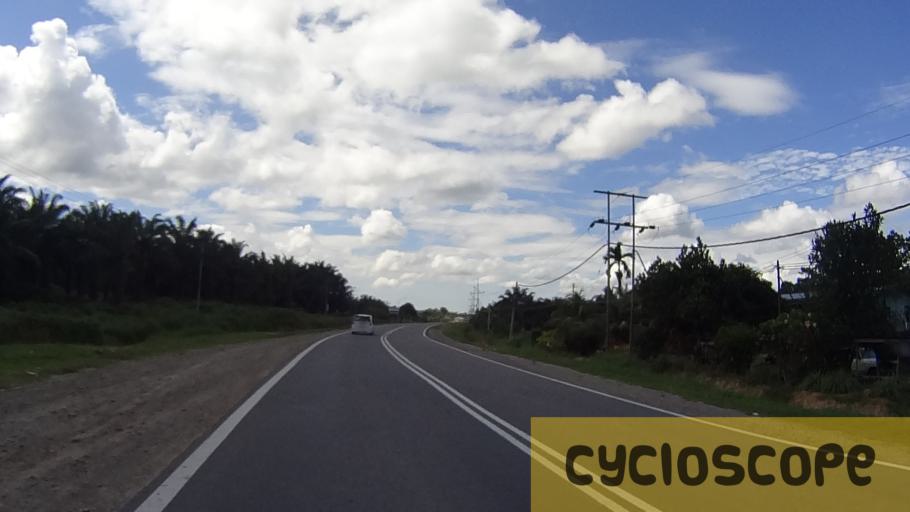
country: MY
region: Sabah
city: Beaufort
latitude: 5.2991
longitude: 115.6953
